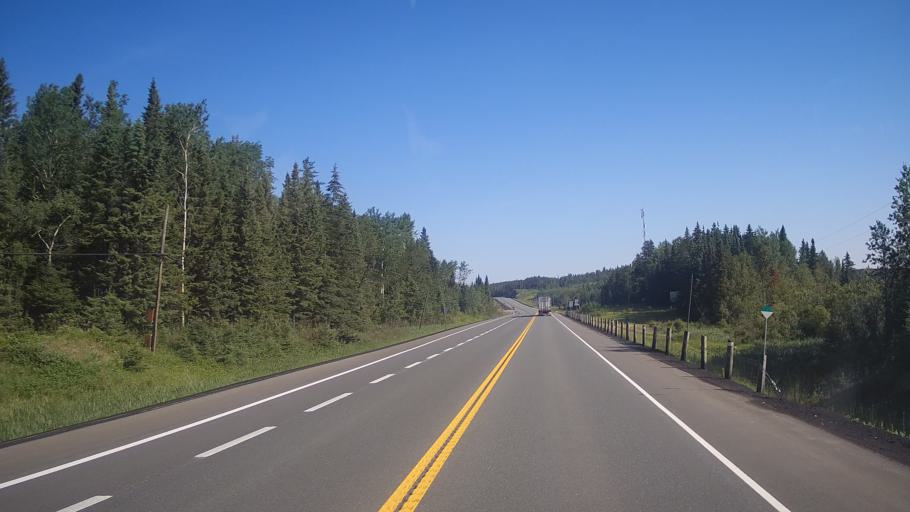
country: CA
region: Ontario
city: Dryden
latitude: 49.6316
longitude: -92.4400
